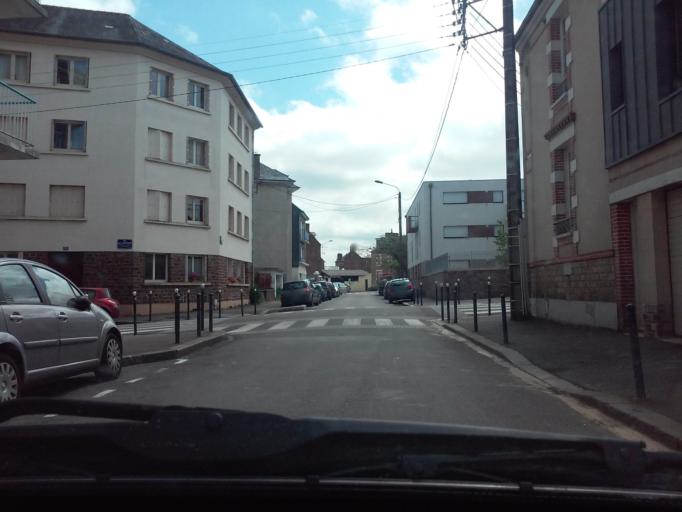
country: FR
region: Brittany
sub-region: Departement d'Ille-et-Vilaine
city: Rennes
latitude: 48.1003
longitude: -1.6834
